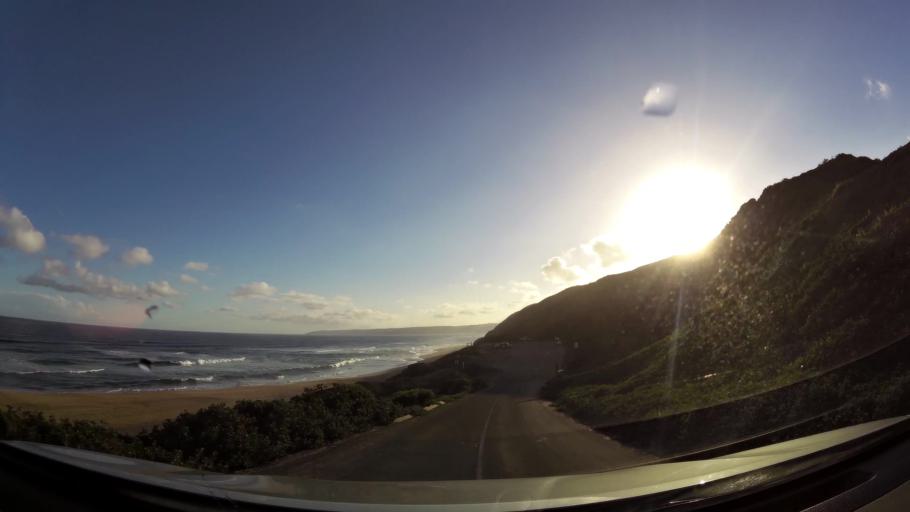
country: ZA
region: Western Cape
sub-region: Eden District Municipality
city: George
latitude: -34.0037
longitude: 22.6459
